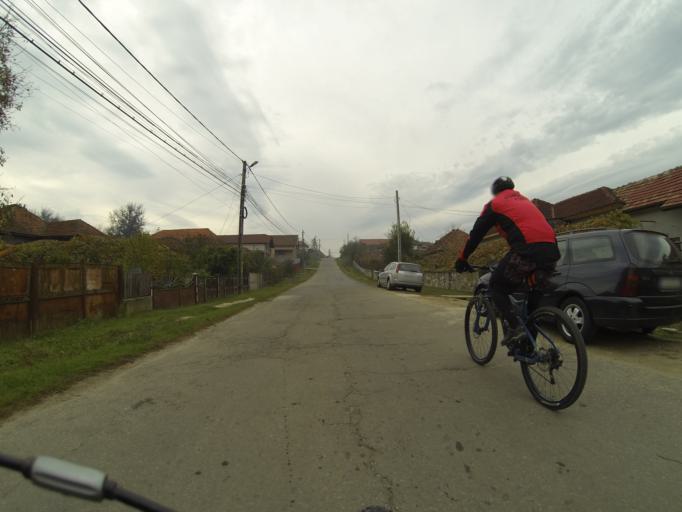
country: RO
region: Gorj
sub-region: Comuna Tismana
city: Pocruia
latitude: 45.0433
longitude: 22.9226
